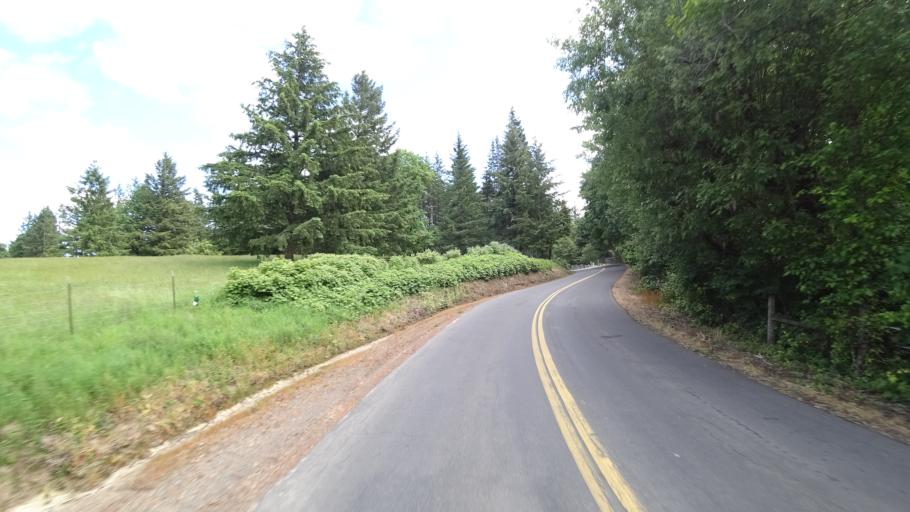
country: US
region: Oregon
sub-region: Washington County
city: Bethany
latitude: 45.6138
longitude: -122.8341
